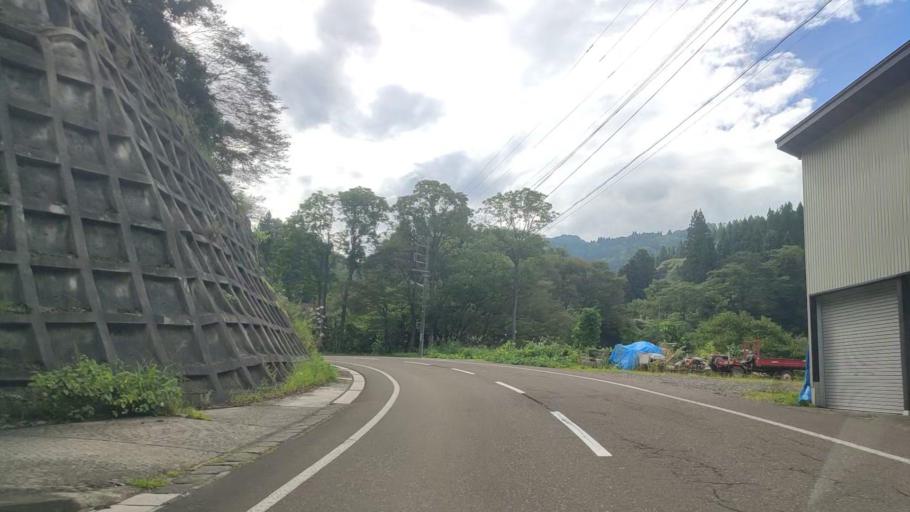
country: JP
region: Niigata
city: Arai
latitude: 36.9321
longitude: 138.2977
